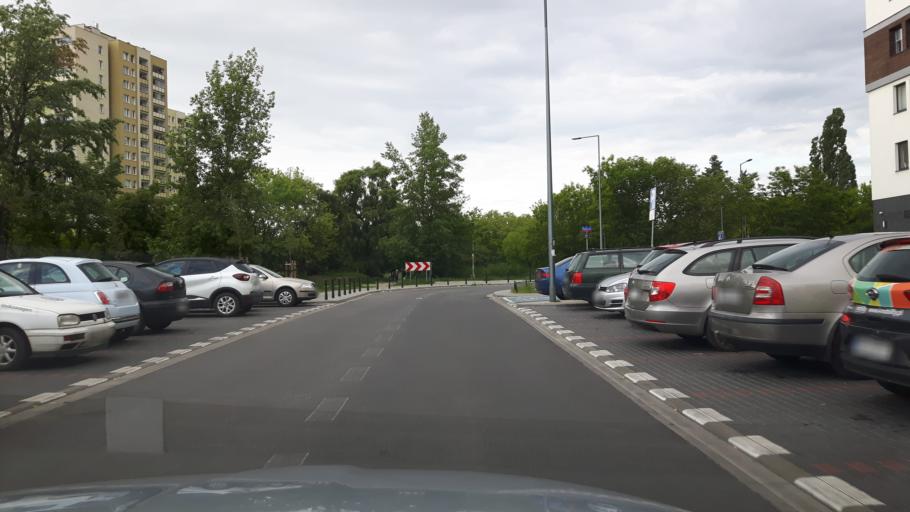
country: PL
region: Masovian Voivodeship
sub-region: Warszawa
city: Praga Poludnie
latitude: 52.2371
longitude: 21.1136
